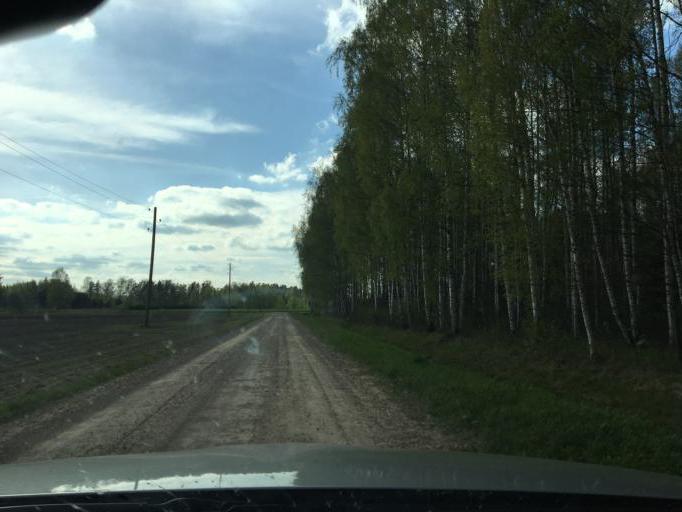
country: LV
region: Ozolnieku
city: Ozolnieki
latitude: 56.6733
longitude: 23.8651
